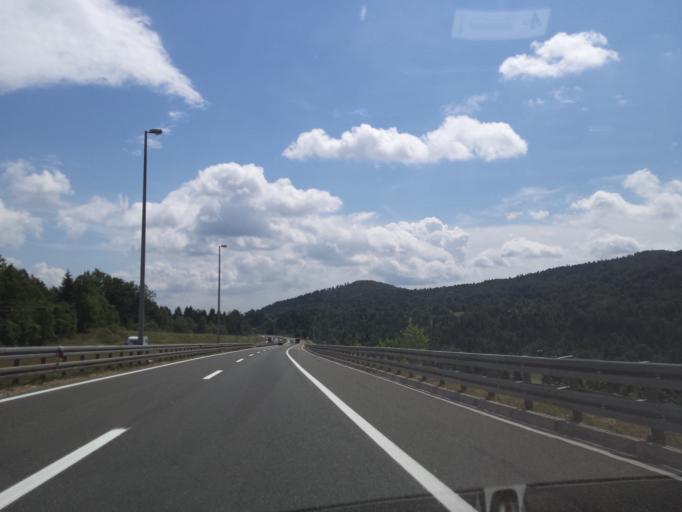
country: HR
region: Primorsko-Goranska
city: Vrbovsko
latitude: 45.3745
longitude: 15.0161
